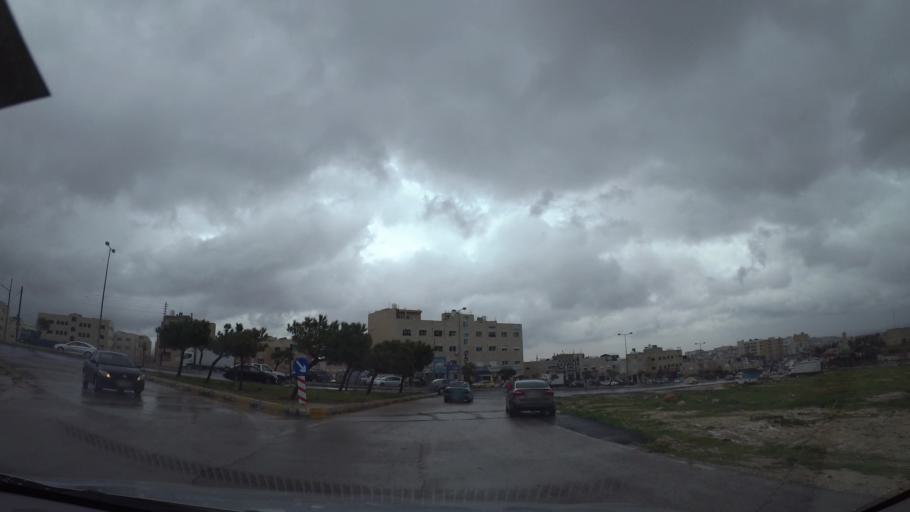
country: JO
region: Amman
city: Al Jubayhah
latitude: 32.0451
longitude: 35.8955
